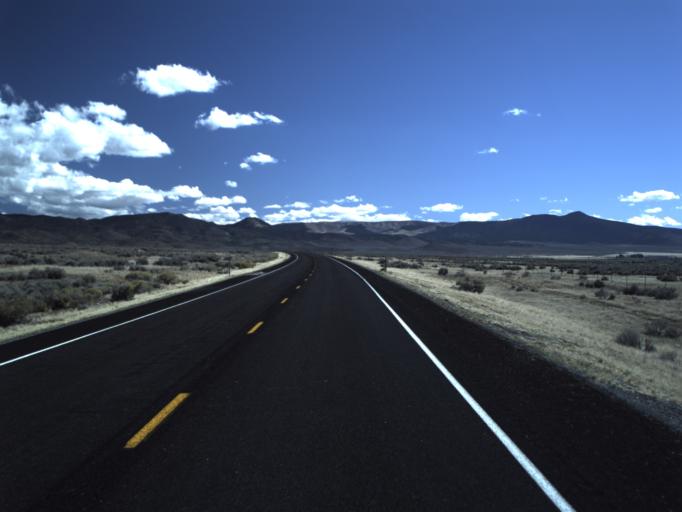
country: US
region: Utah
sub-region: Beaver County
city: Milford
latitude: 38.2564
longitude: -112.9499
